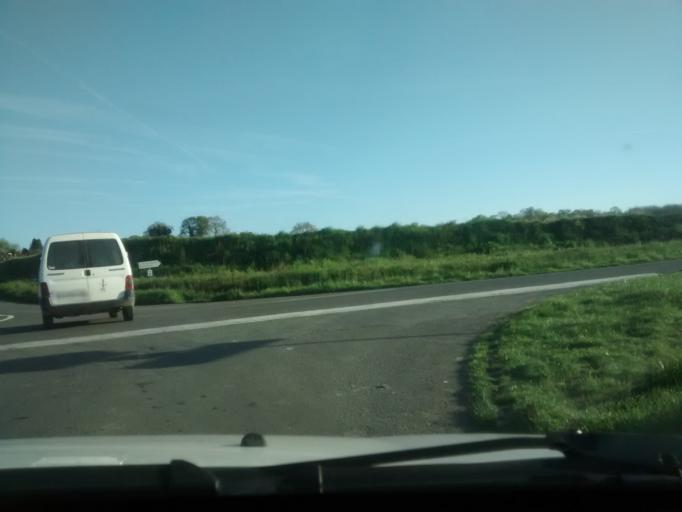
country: FR
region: Brittany
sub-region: Departement d'Ille-et-Vilaine
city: Pleine-Fougeres
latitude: 48.5496
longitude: -1.5797
